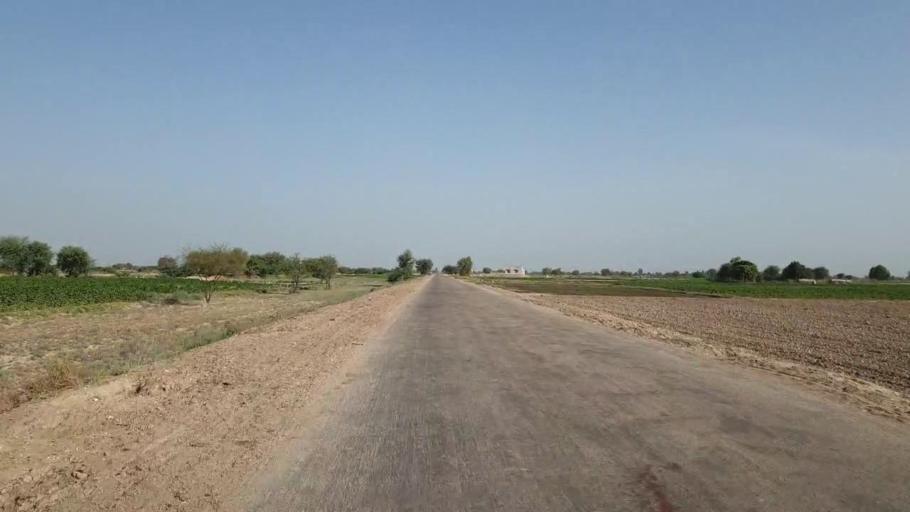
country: PK
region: Sindh
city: Nawabshah
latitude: 26.1446
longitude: 68.4504
